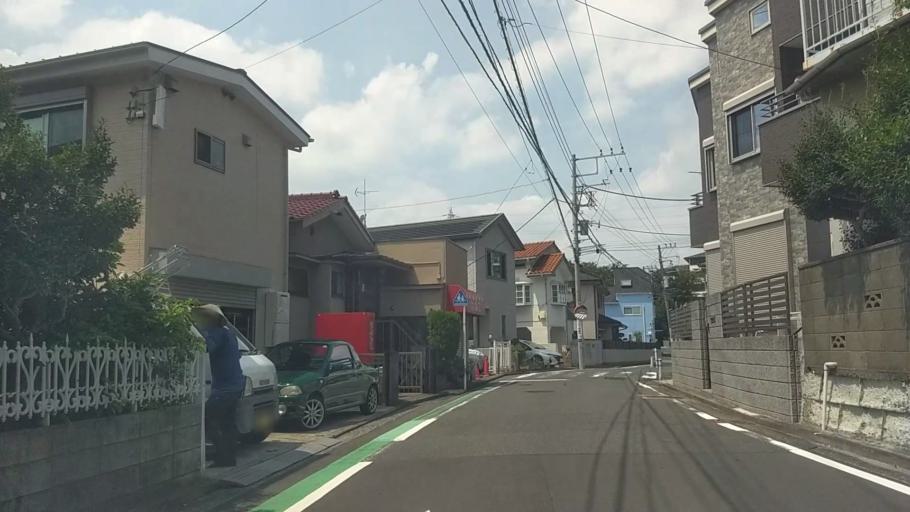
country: JP
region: Kanagawa
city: Yokohama
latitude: 35.4909
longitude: 139.6172
